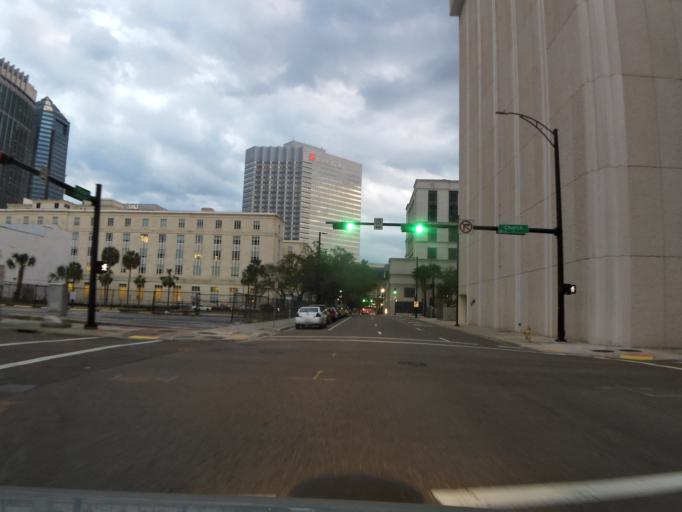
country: US
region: Florida
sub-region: Duval County
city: Jacksonville
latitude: 30.3312
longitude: -81.6619
